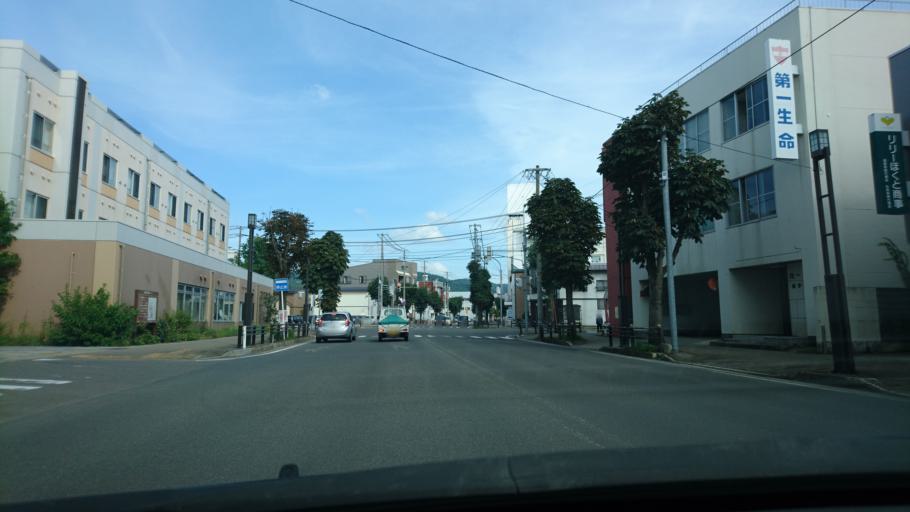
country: JP
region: Akita
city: Yokotemachi
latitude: 39.3104
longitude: 140.5622
